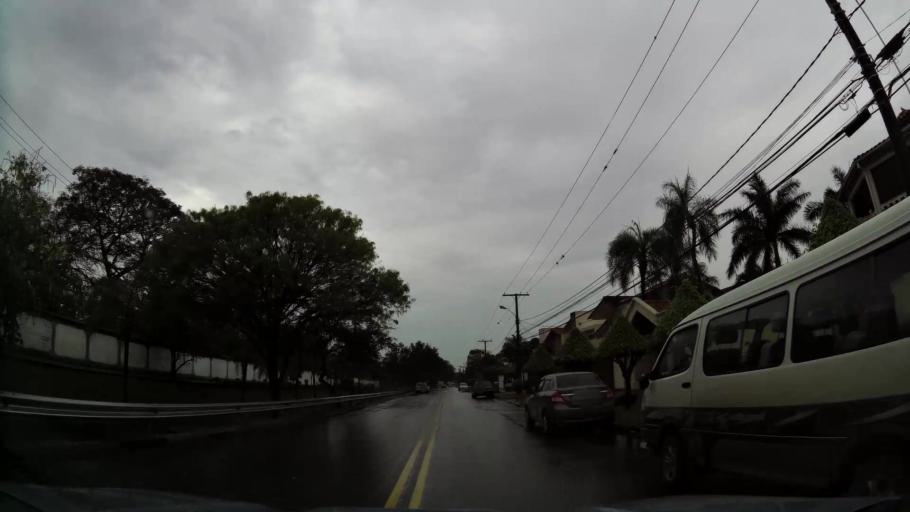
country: BO
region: Santa Cruz
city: Santa Cruz de la Sierra
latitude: -17.8025
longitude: -63.2024
